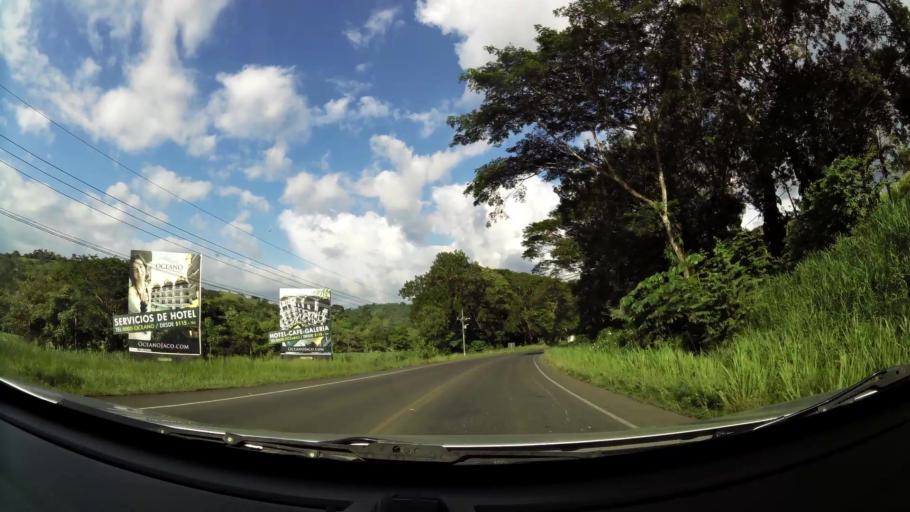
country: CR
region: Puntarenas
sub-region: Canton de Garabito
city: Jaco
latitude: 9.7209
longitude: -84.6313
